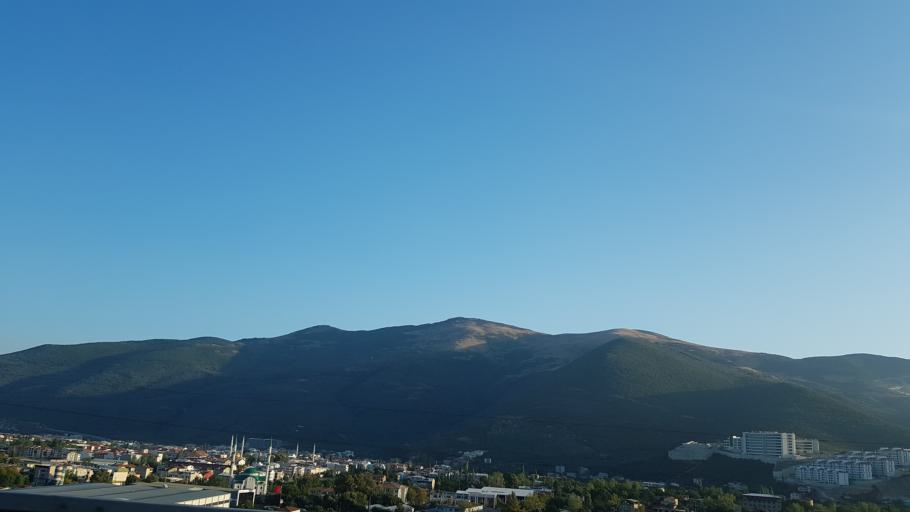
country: TR
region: Bursa
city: Umurbey
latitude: 40.4218
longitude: 29.1822
